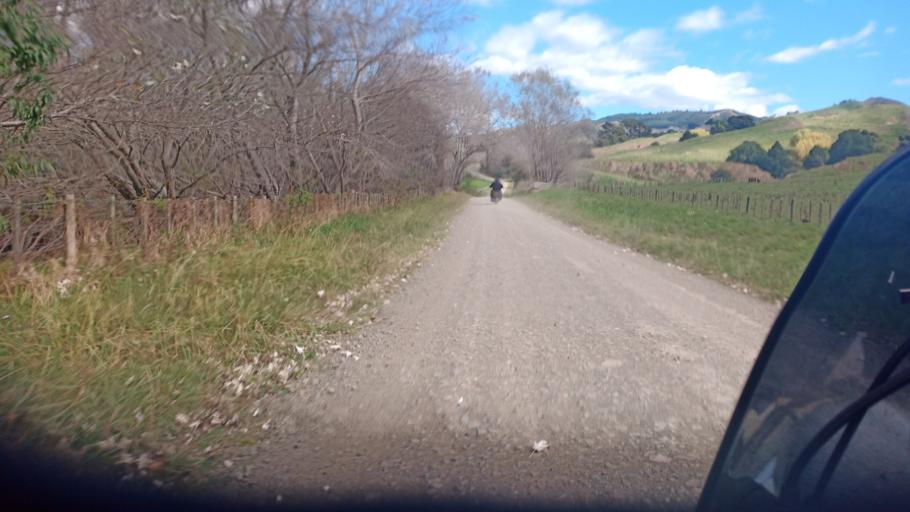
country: NZ
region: Gisborne
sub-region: Gisborne District
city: Gisborne
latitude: -38.4236
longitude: 177.7207
